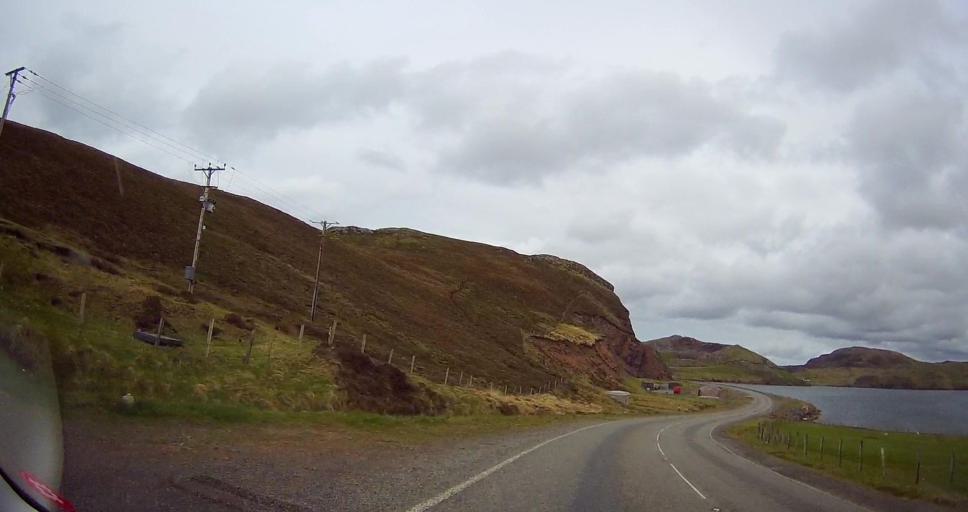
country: GB
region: Scotland
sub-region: Shetland Islands
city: Lerwick
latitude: 60.3924
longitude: -1.3769
